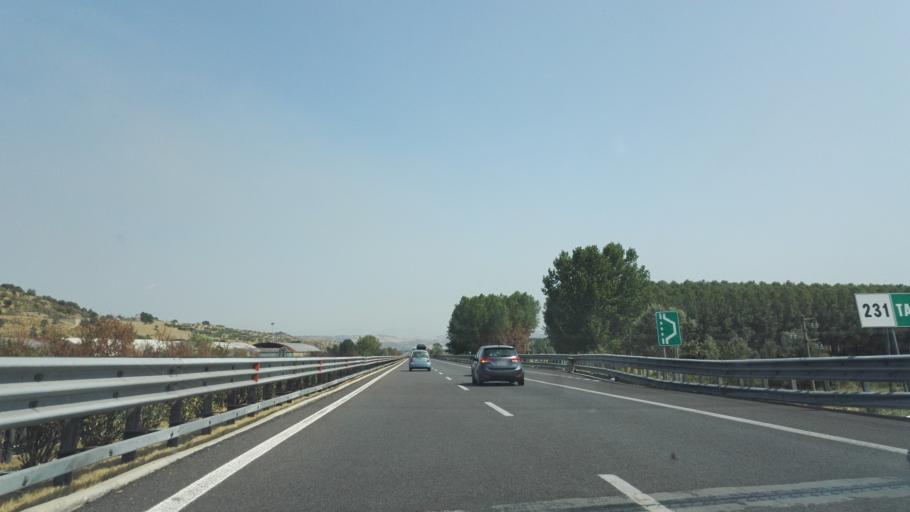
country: IT
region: Calabria
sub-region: Provincia di Cosenza
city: Sartano
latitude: 39.5383
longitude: 16.2240
